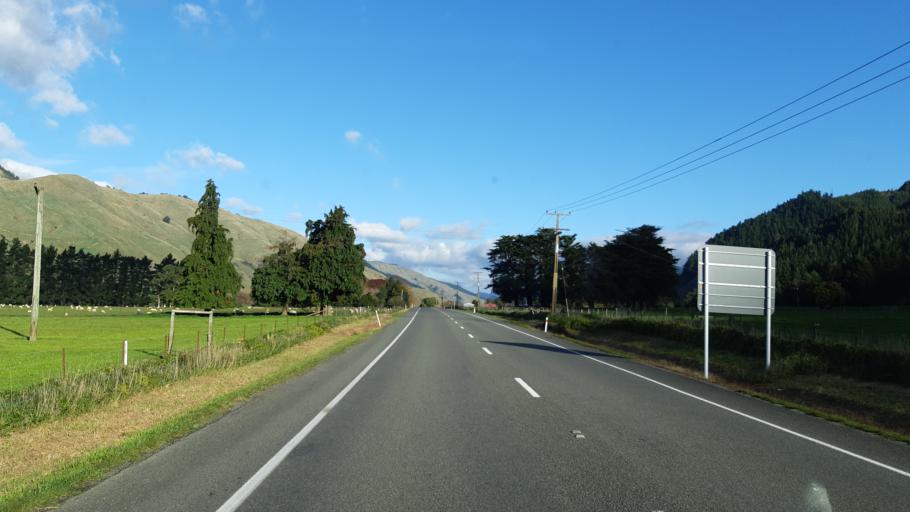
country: NZ
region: Marlborough
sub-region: Marlborough District
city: Picton
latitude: -41.2987
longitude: 173.7703
